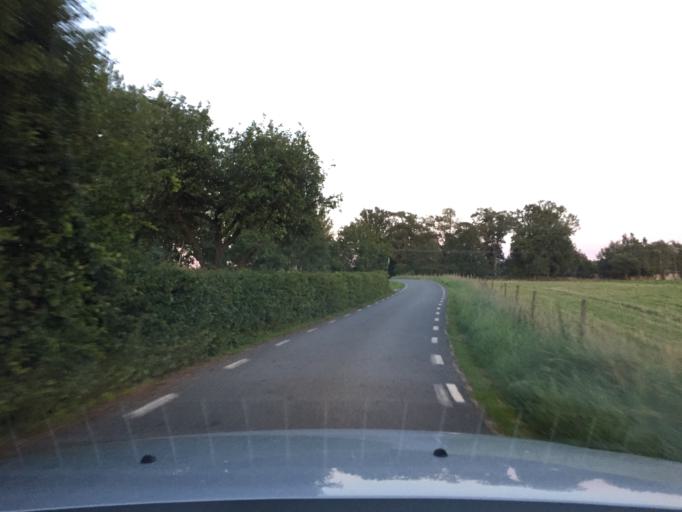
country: SE
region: Skane
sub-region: Hassleholms Kommun
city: Sosdala
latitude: 55.9827
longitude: 13.6870
